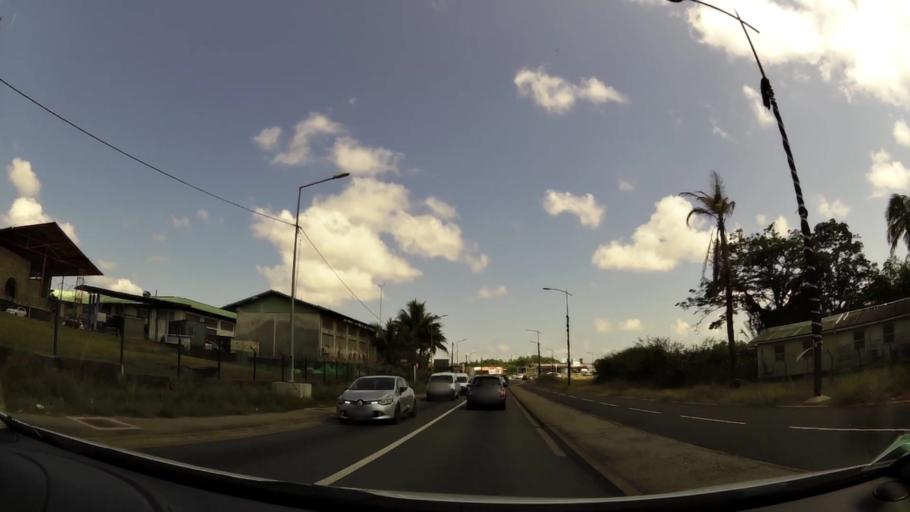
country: GF
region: Guyane
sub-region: Guyane
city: Cayenne
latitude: 4.9223
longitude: -52.3230
